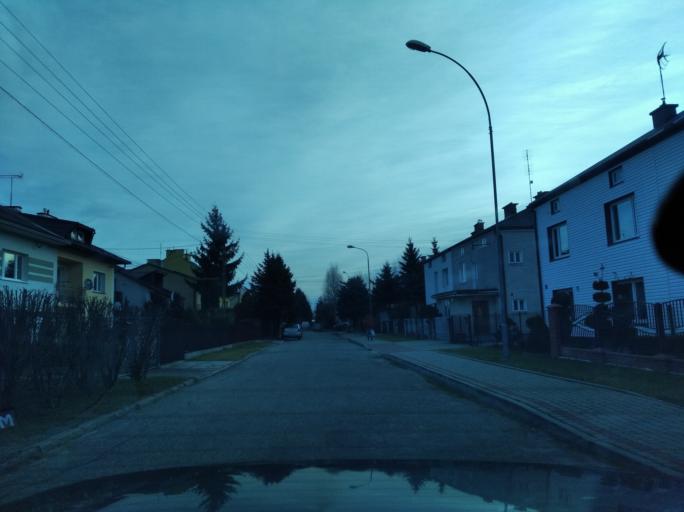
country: PL
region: Subcarpathian Voivodeship
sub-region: Powiat ropczycko-sedziszowski
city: Sedziszow Malopolski
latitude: 50.0734
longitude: 21.6971
